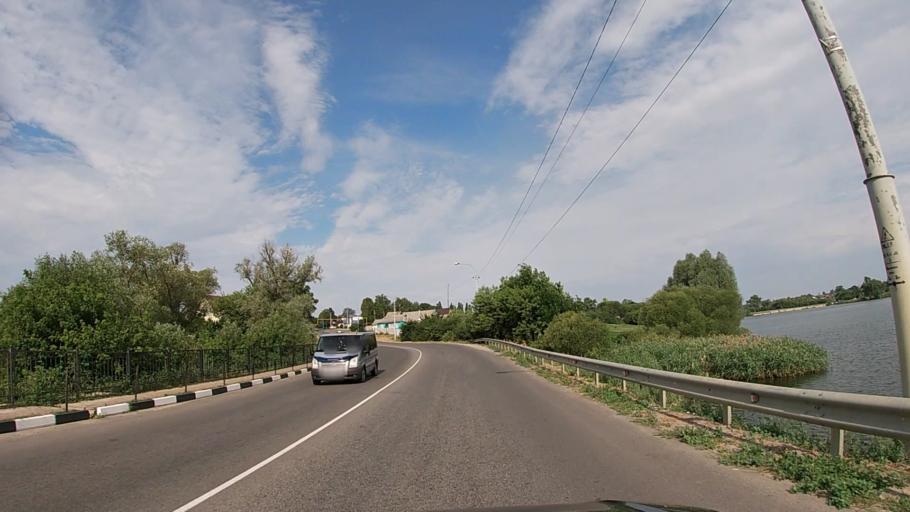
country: RU
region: Belgorod
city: Krasnaya Yaruga
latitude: 50.8012
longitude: 35.6696
